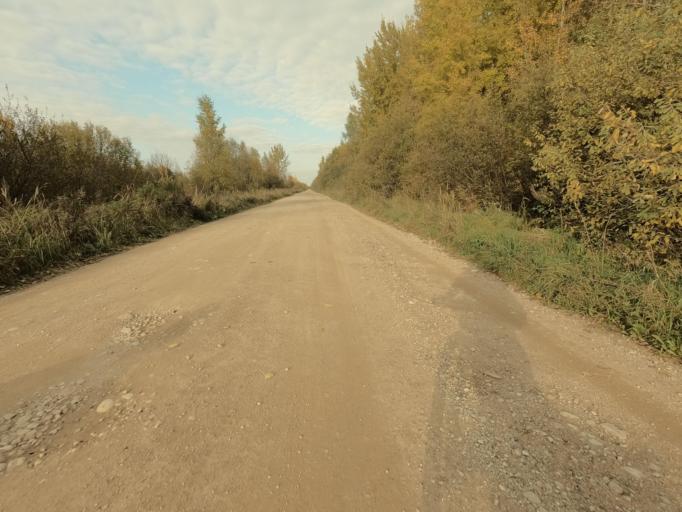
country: RU
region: Novgorod
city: Volkhovskiy
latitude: 58.9063
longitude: 31.0368
